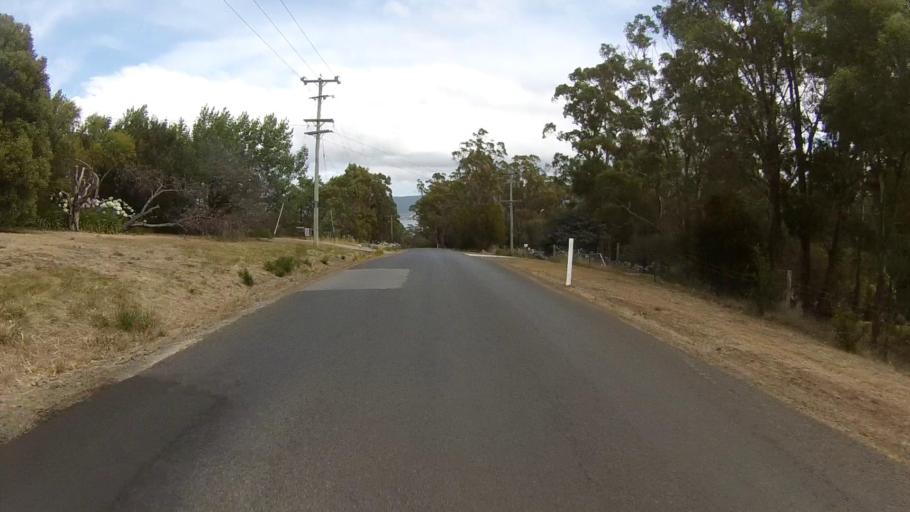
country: AU
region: Tasmania
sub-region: Kingborough
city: Blackmans Bay
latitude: -43.0317
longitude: 147.3102
